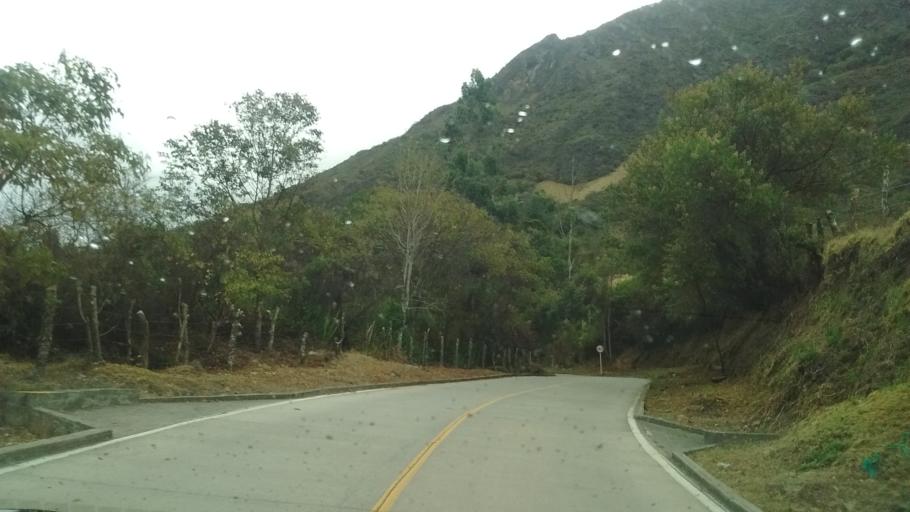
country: CO
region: Cauca
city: La Vega
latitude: 2.0089
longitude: -76.7872
